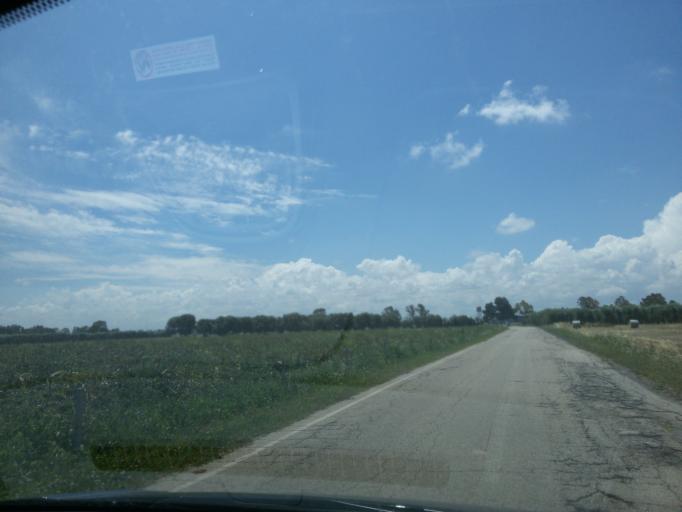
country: IT
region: Apulia
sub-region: Provincia di Brindisi
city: Brindisi
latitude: 40.6531
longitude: 17.8387
